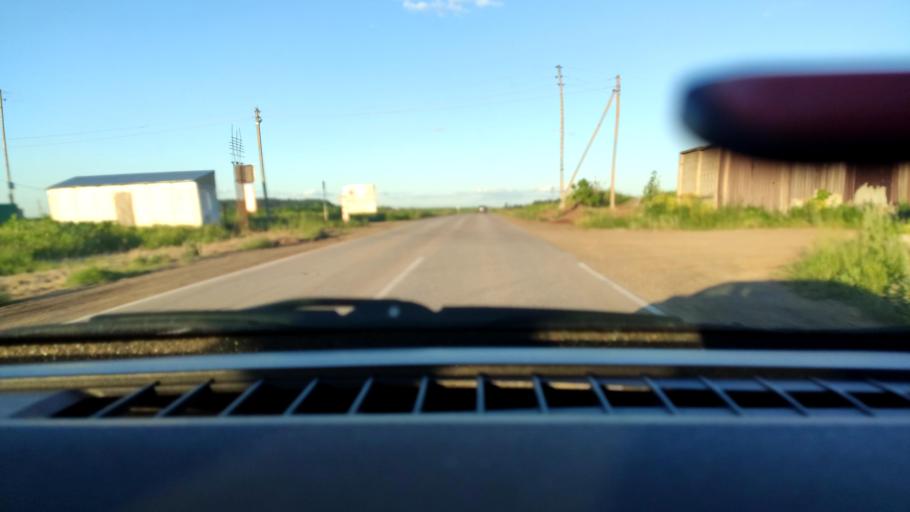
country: RU
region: Perm
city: Kultayevo
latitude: 57.9238
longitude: 55.9080
